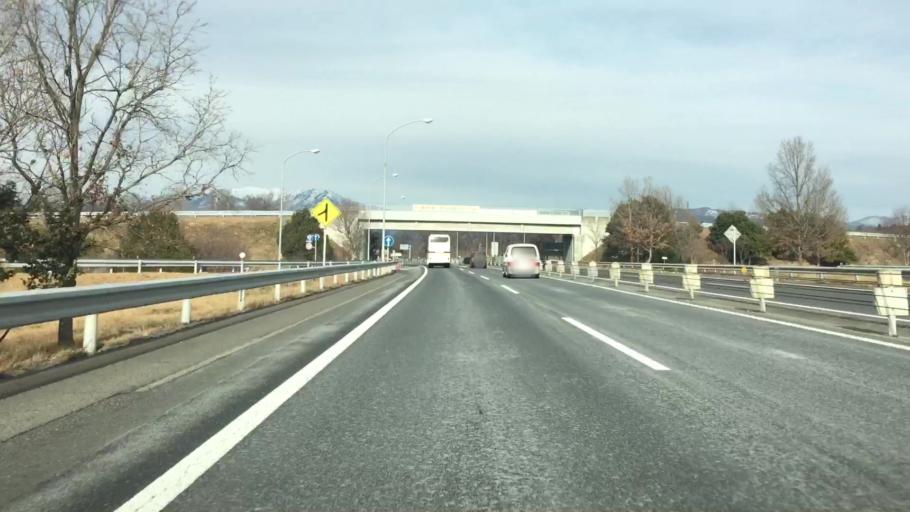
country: JP
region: Gunma
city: Numata
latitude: 36.6147
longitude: 139.0666
